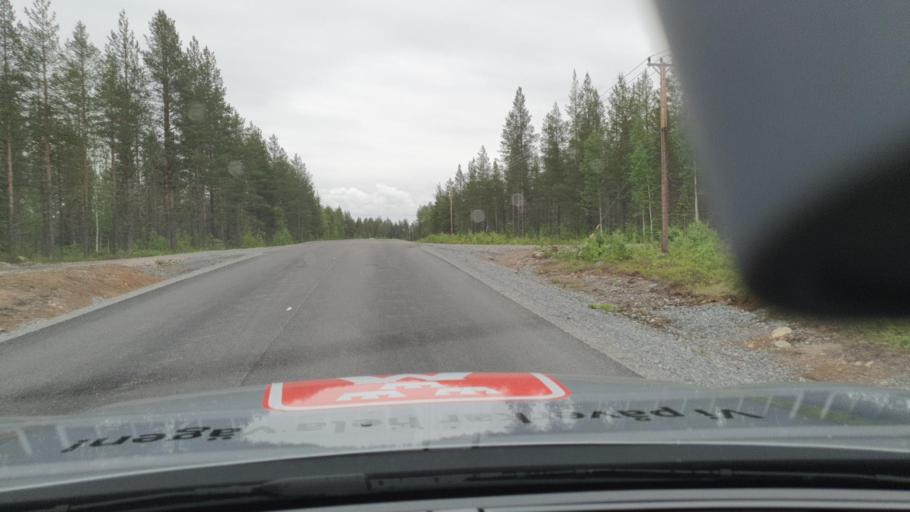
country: SE
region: Norrbotten
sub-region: Overtornea Kommun
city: OEvertornea
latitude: 66.6389
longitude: 23.2556
